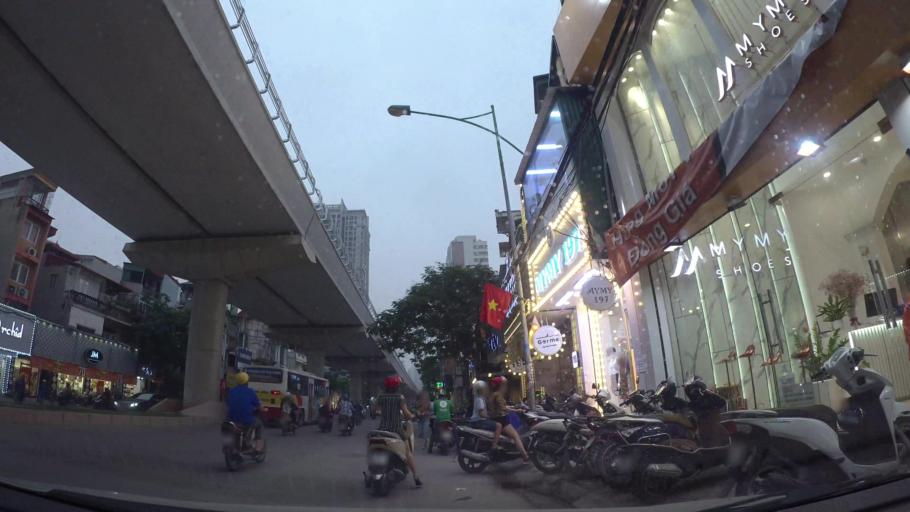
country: VN
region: Ha Noi
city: Cau Giay
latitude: 21.0333
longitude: 105.7977
